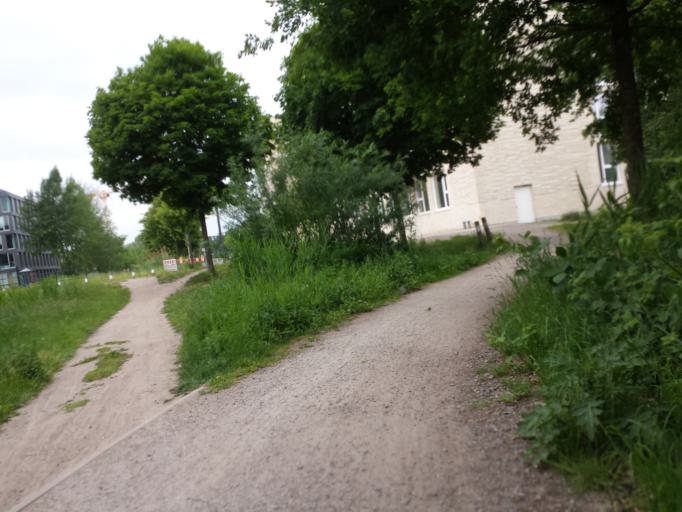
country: DE
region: Bremen
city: Bremen
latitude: 53.1047
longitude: 8.8620
